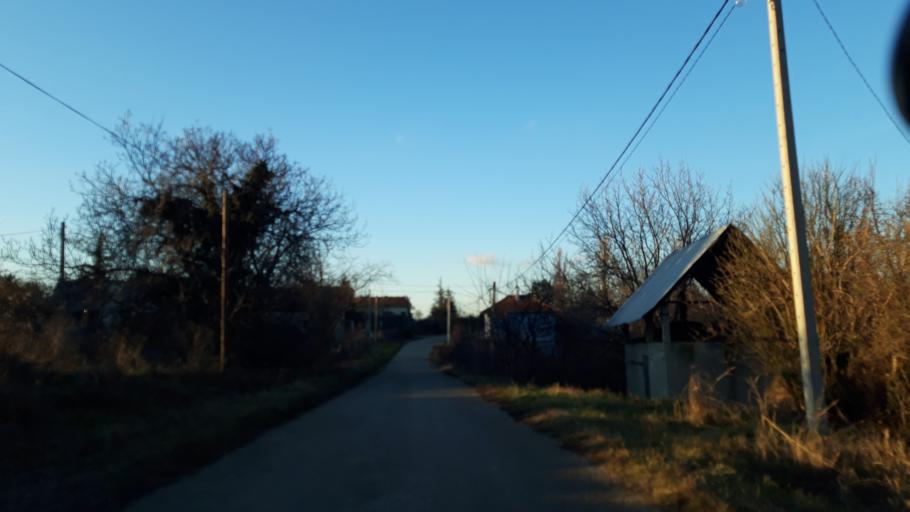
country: RS
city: Cortanovci
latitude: 45.1631
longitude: 20.0008
